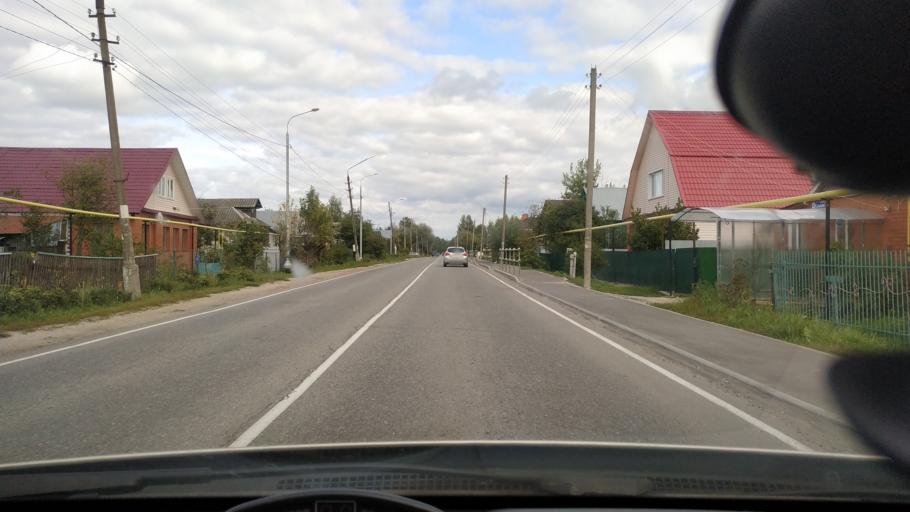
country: RU
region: Moskovskaya
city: Likino-Dulevo
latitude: 55.7297
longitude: 39.0032
